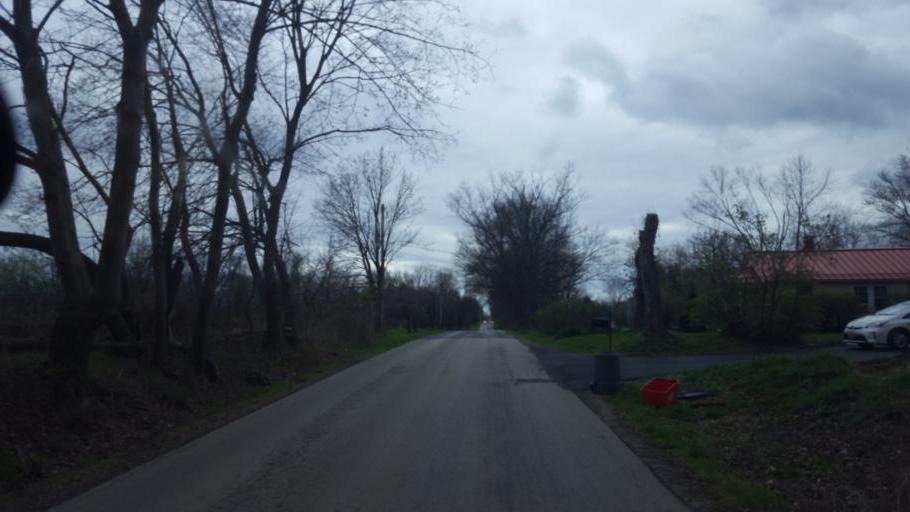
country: US
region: Ohio
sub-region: Franklin County
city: Westerville
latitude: 40.1833
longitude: -82.8989
